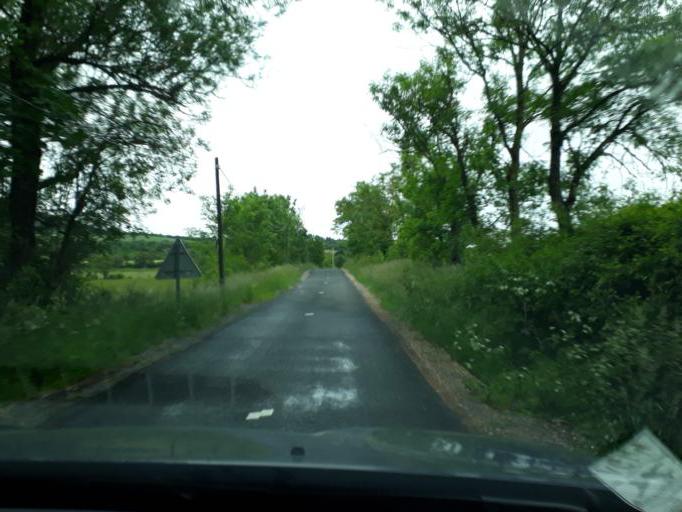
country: FR
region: Languedoc-Roussillon
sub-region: Departement de l'Herault
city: Lodeve
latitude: 43.8385
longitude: 3.2783
